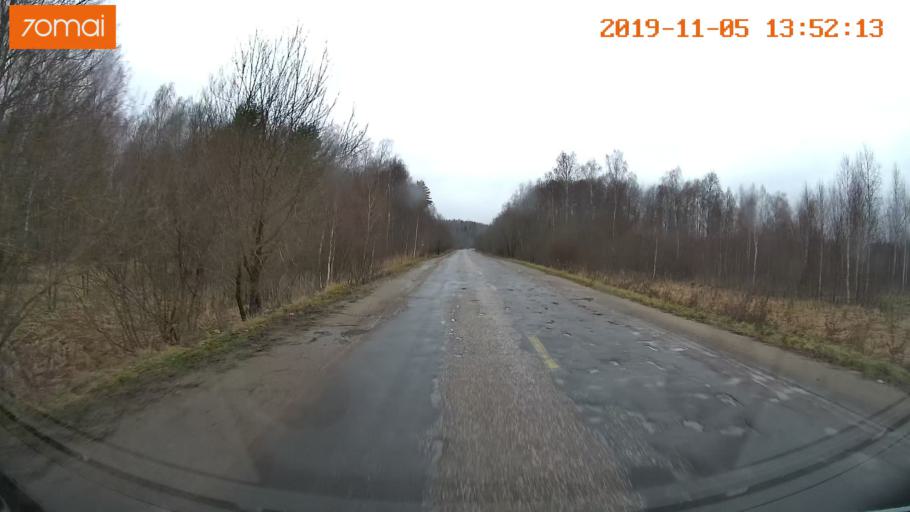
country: RU
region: Ivanovo
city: Kaminskiy
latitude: 57.0269
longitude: 41.3895
